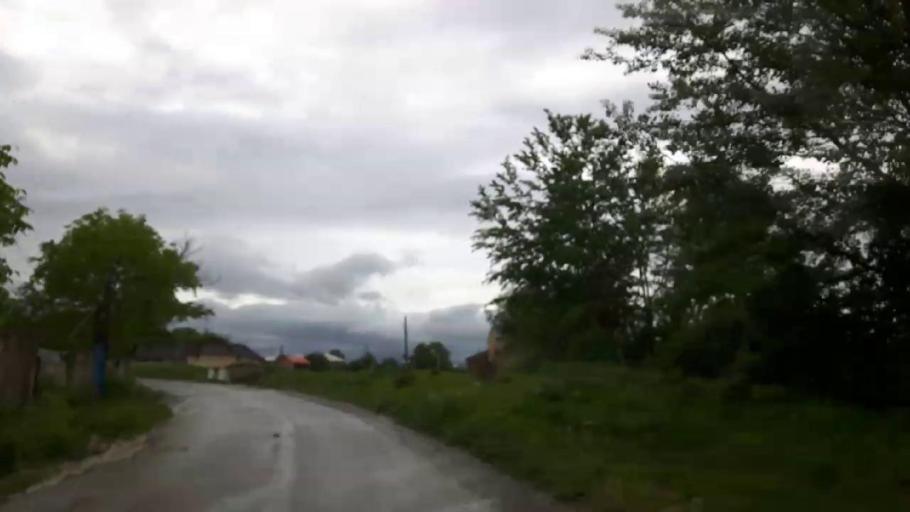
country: GE
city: Agara
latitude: 41.9942
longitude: 43.7349
